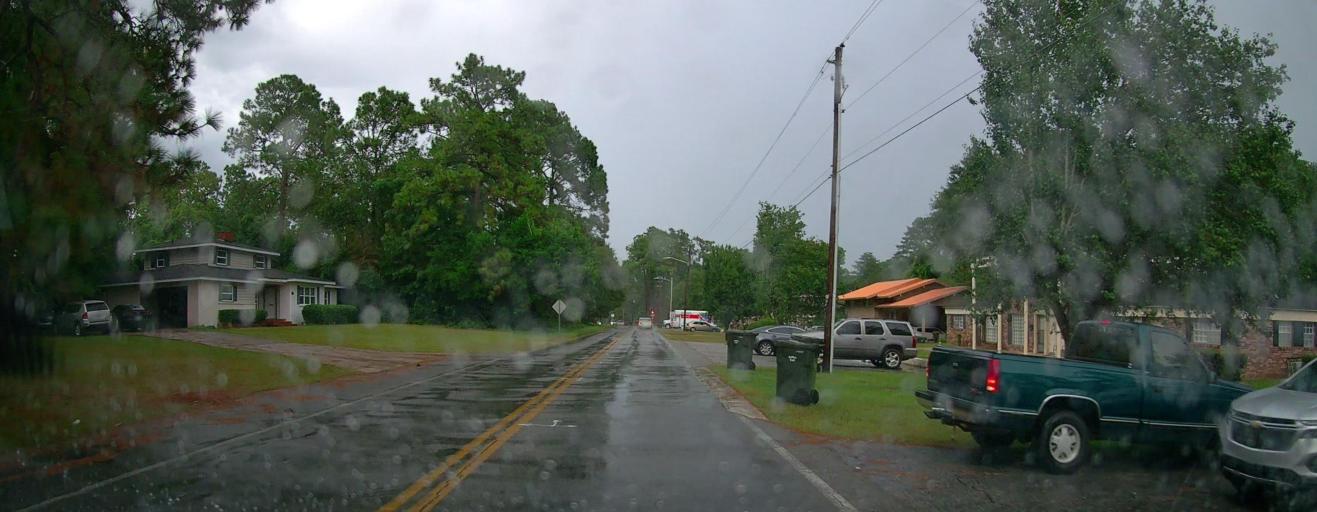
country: US
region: Georgia
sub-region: Ware County
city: Sunnyside
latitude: 31.2208
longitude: -82.3301
